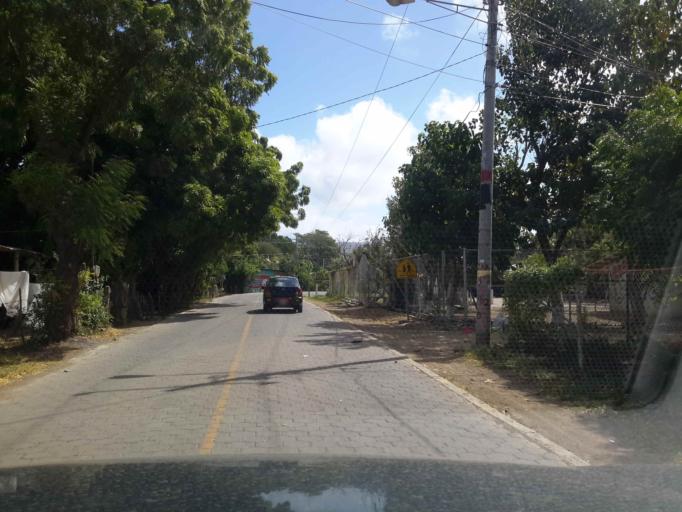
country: NI
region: Rivas
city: San Juan del Sur
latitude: 11.2533
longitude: -85.8531
